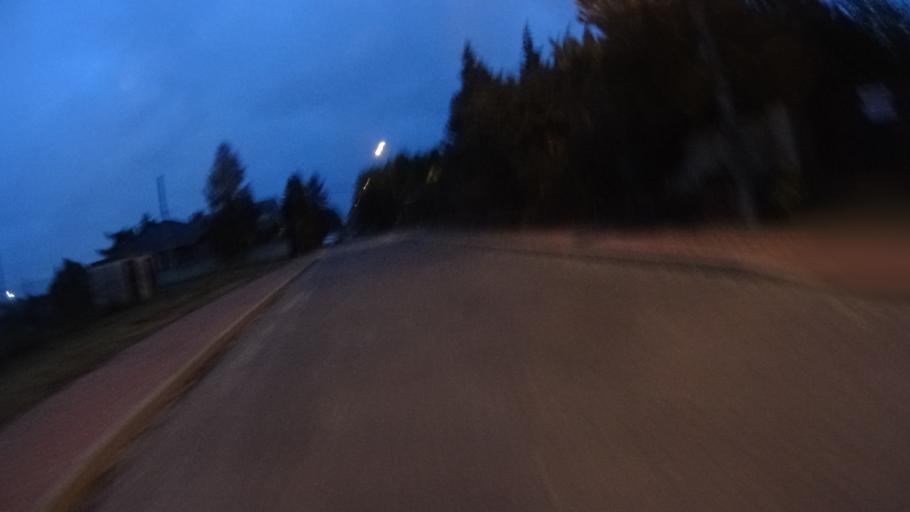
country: PL
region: Masovian Voivodeship
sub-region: Powiat warszawski zachodni
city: Babice
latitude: 52.2278
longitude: 20.8680
